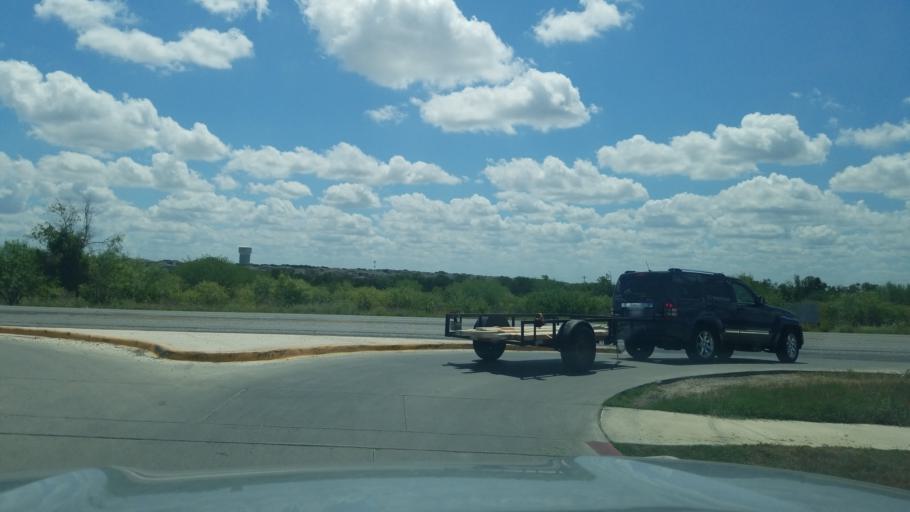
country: US
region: Texas
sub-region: Bexar County
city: Converse
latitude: 29.5282
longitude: -98.3085
